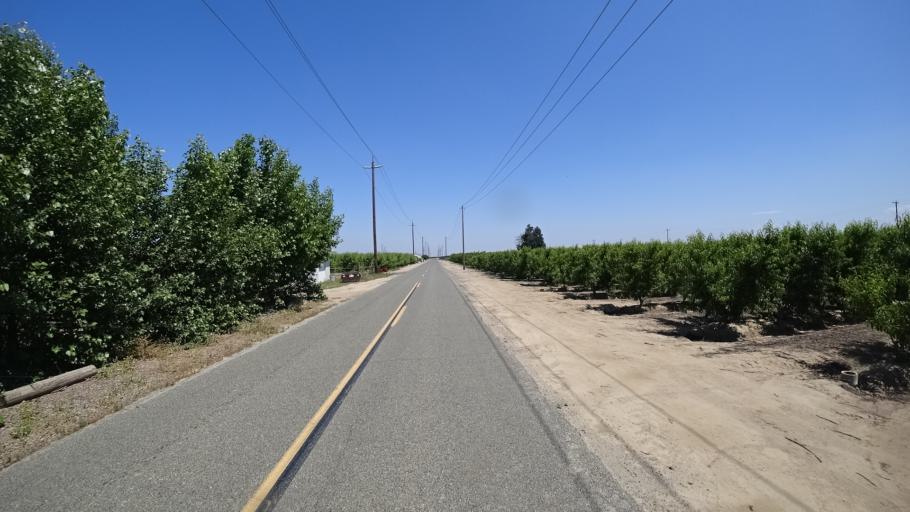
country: US
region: California
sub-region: Fresno County
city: Kingsburg
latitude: 36.4817
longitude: -119.5820
